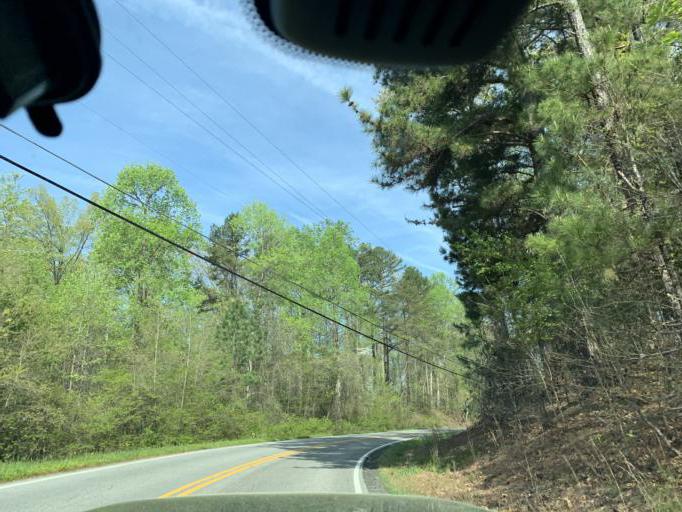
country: US
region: Georgia
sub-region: Forsyth County
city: Cumming
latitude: 34.2084
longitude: -84.0722
